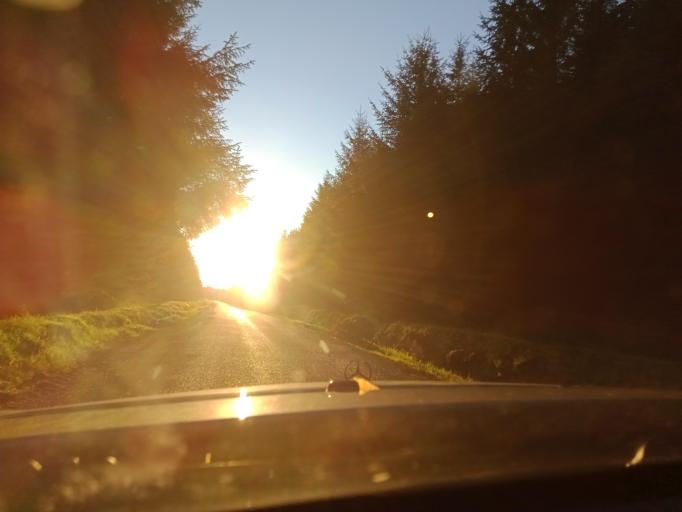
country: IE
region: Munster
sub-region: Waterford
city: Waterford
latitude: 52.3726
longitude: -7.1032
